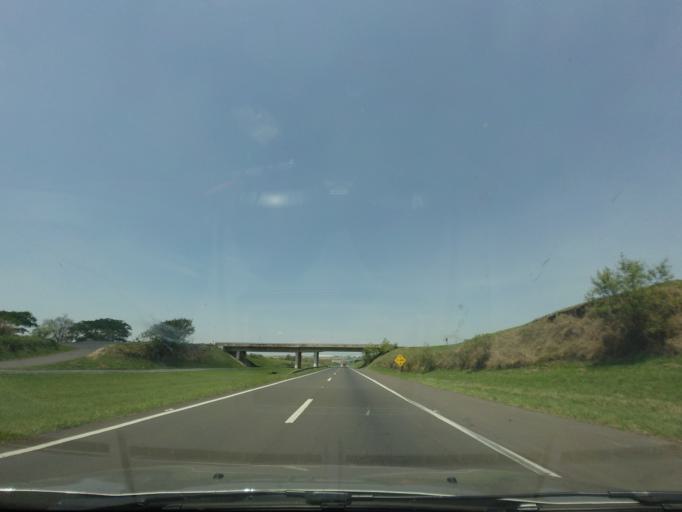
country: BR
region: Sao Paulo
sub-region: Santa Barbara D'Oeste
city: Santa Barbara d'Oeste
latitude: -22.7476
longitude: -47.5058
